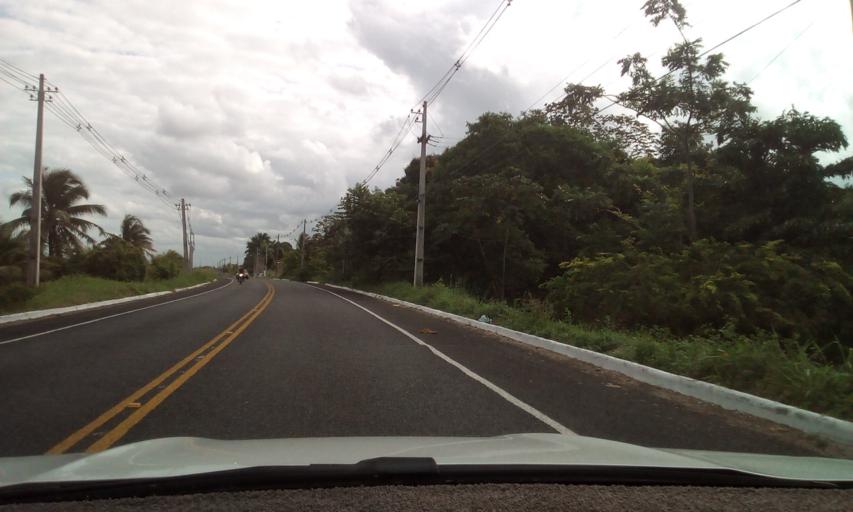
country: BR
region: Paraiba
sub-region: Rio Tinto
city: Rio Tinto
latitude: -6.8137
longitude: -35.0927
